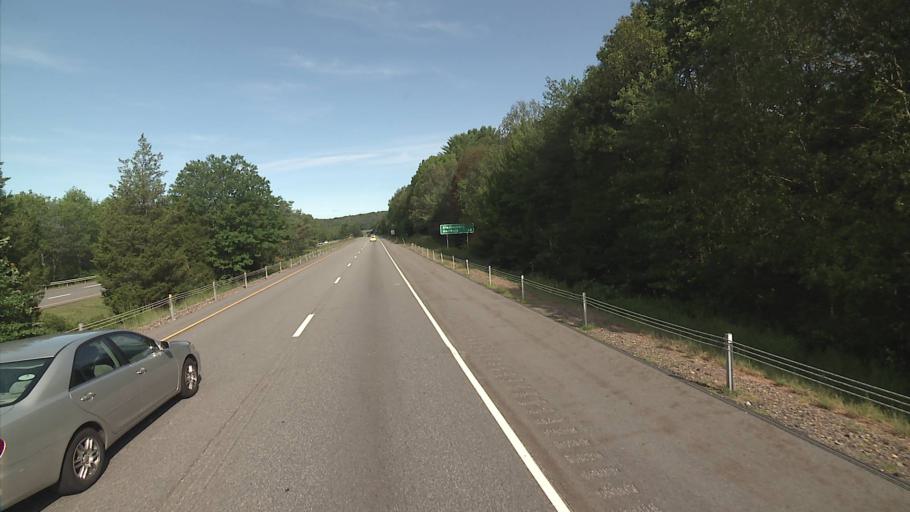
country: US
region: Connecticut
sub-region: New London County
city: Colchester
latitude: 41.5770
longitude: -72.3507
